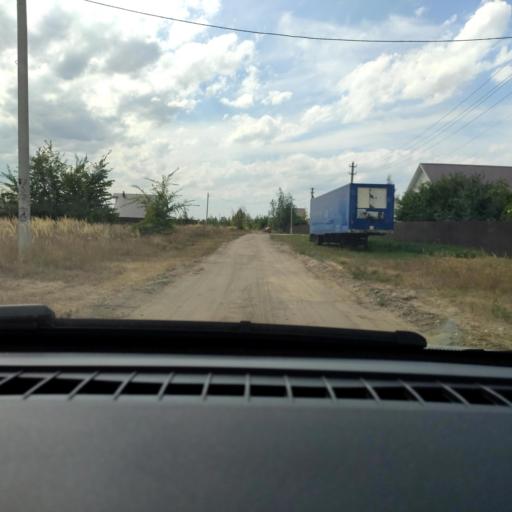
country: RU
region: Voronezj
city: Novaya Usman'
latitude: 51.6668
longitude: 39.4417
